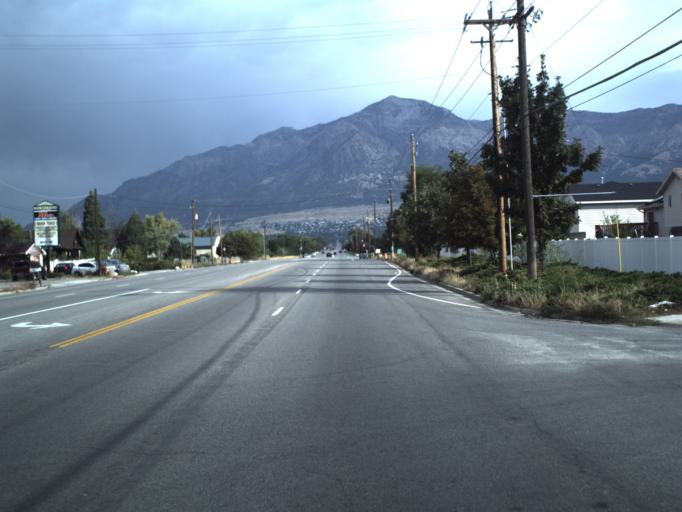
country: US
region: Utah
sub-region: Weber County
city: Harrisville
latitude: 41.2783
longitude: -111.9692
